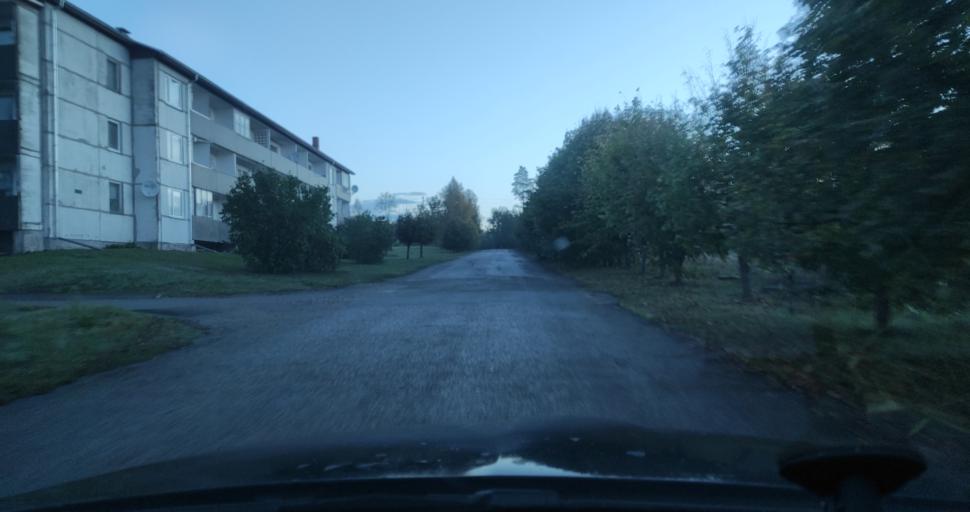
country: LV
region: Kuldigas Rajons
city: Kuldiga
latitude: 56.8835
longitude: 21.8237
